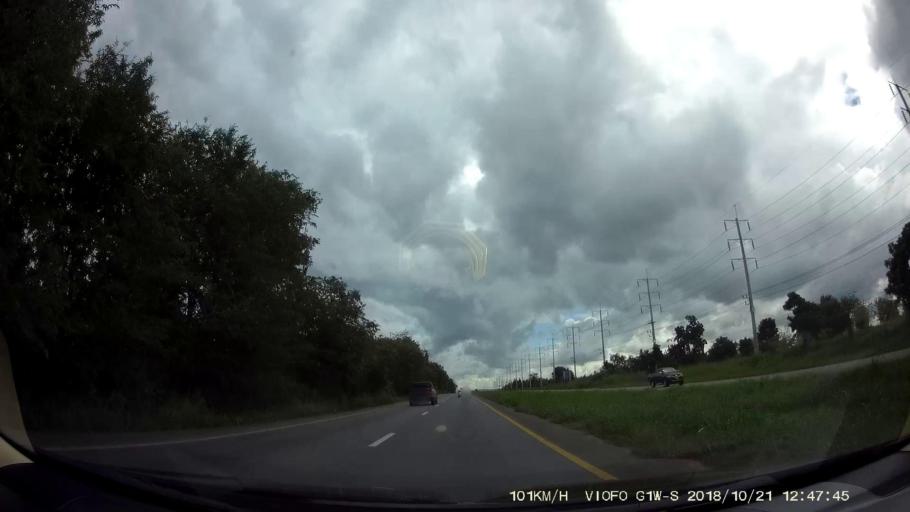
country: TH
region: Nakhon Ratchasima
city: Amphoe Sikhiu
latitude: 14.9237
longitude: 101.6840
